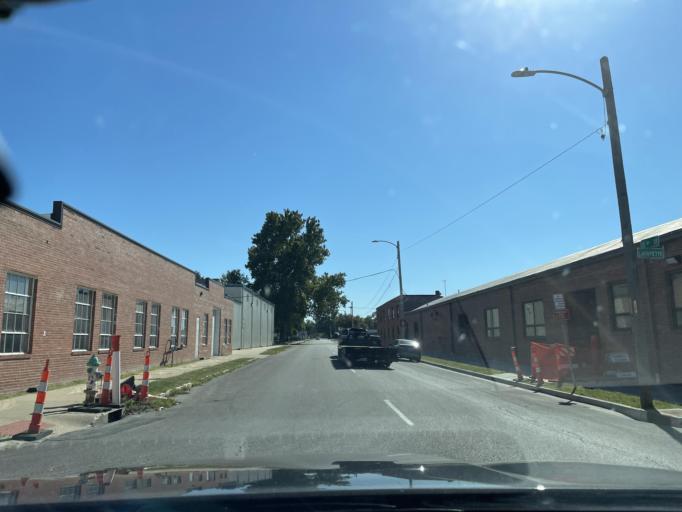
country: US
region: Missouri
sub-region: Buchanan County
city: Saint Joseph
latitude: 39.7581
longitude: -94.8493
